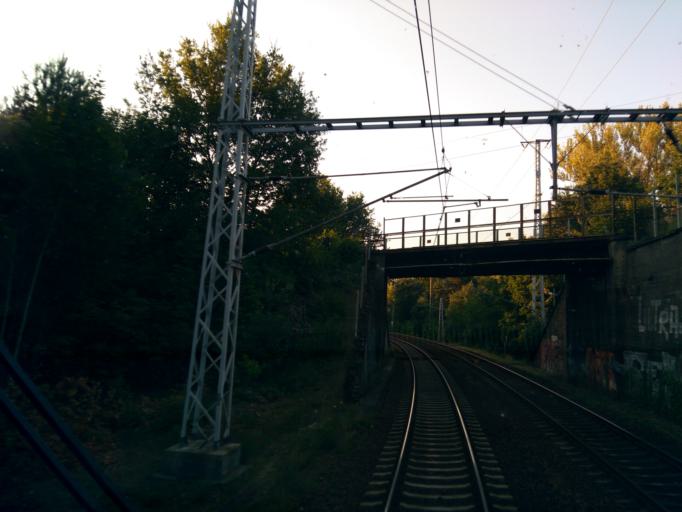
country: DE
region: Berlin
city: Adlershof
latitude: 52.4186
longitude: 13.5589
